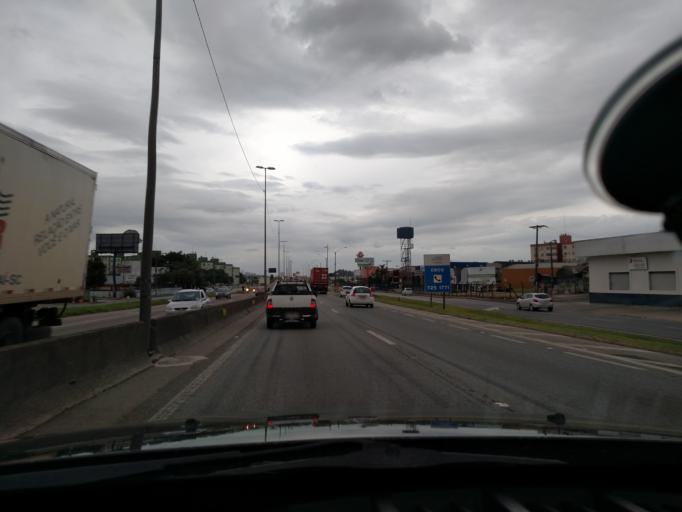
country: BR
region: Santa Catarina
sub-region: Sao Jose
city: Campinas
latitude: -27.5705
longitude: -48.6137
